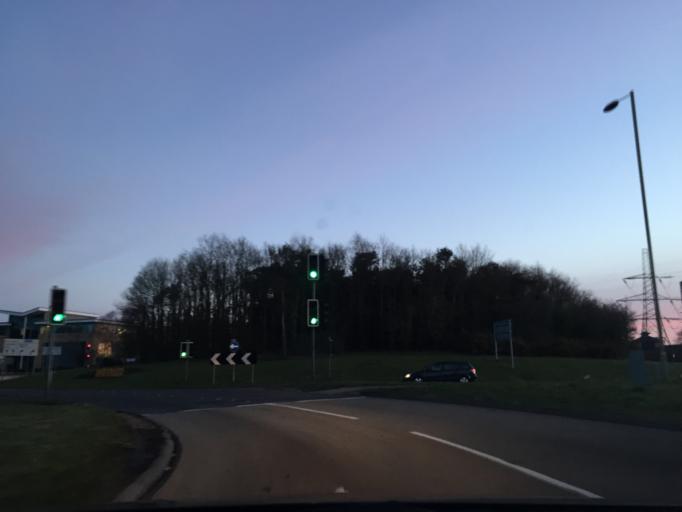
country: GB
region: England
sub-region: Hampshire
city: Botley
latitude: 50.8679
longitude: -1.2553
